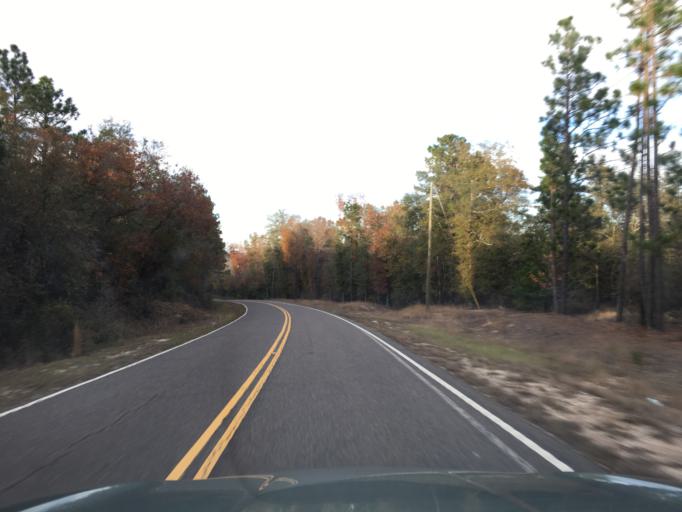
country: US
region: South Carolina
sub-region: Lexington County
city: Red Bank
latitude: 33.7143
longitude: -81.3551
